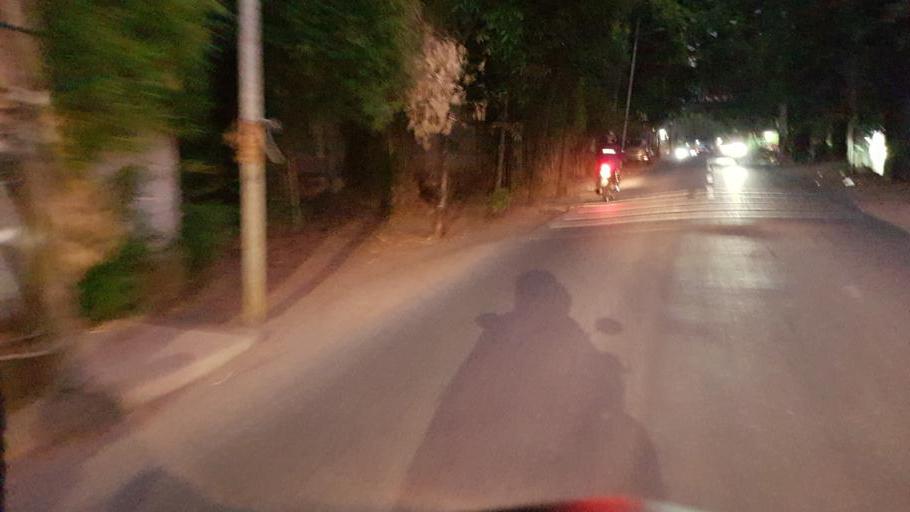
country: ID
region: Jakarta Raya
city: Jakarta
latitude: -6.2981
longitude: 106.8263
